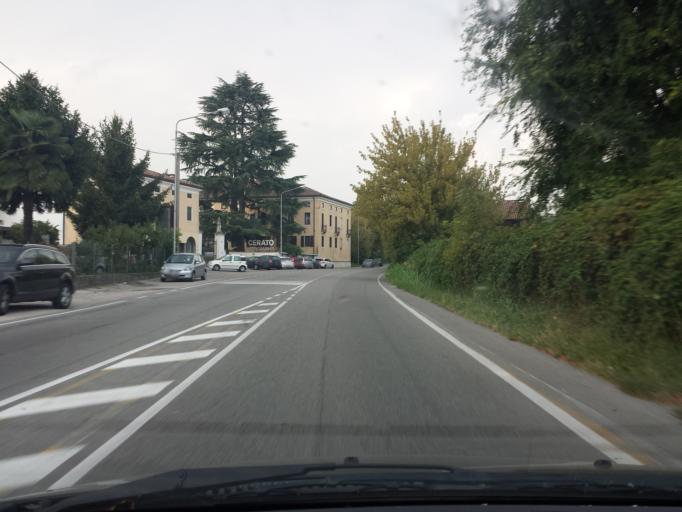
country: IT
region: Veneto
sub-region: Provincia di Vicenza
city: Monticello Conte Otto
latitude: 45.5788
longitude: 11.5525
